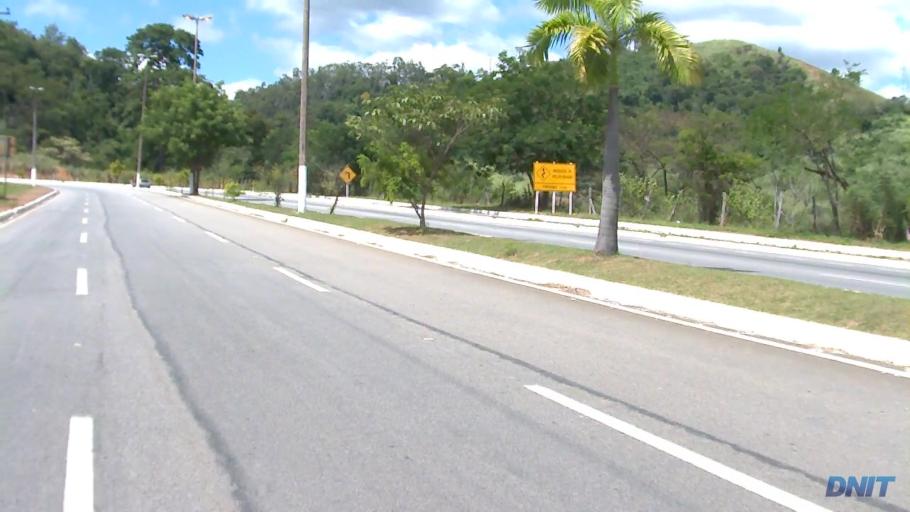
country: BR
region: Minas Gerais
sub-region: Coronel Fabriciano
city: Coronel Fabriciano
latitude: -19.5048
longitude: -42.5949
